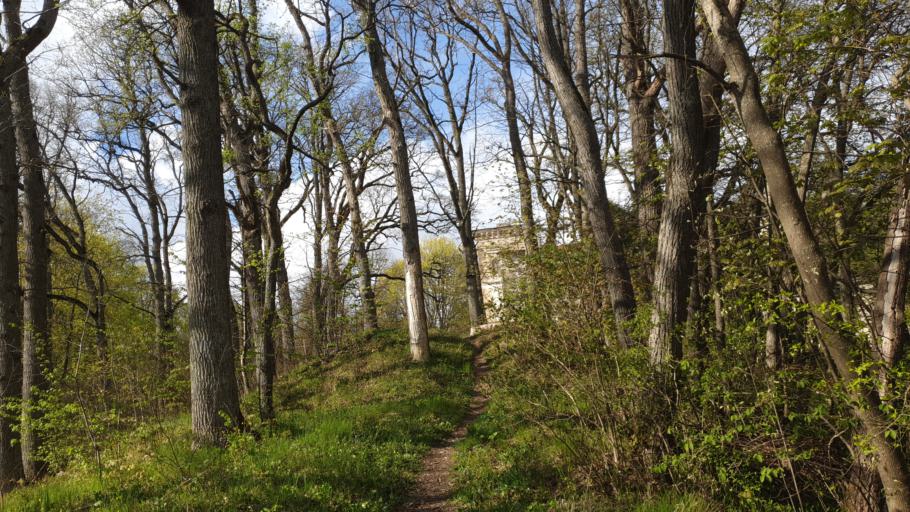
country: LT
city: Vilkija
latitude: 55.0791
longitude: 23.3902
